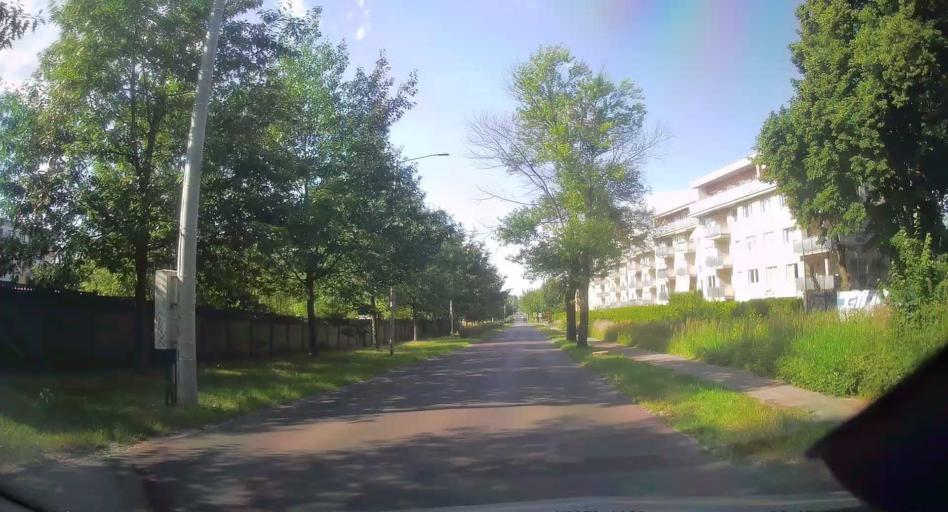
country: PL
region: Silesian Voivodeship
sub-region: Czestochowa
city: Czestochowa
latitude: 50.8195
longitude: 19.0990
